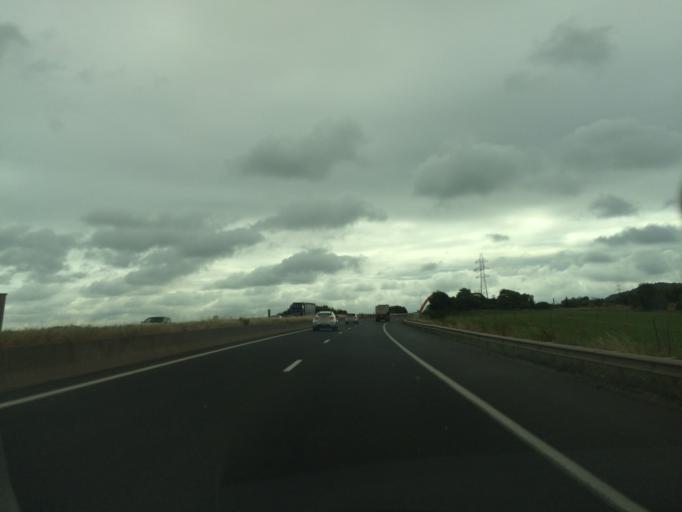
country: LU
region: Luxembourg
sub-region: Canton d'Esch-sur-Alzette
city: Schifflange
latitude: 49.5121
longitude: 6.0291
